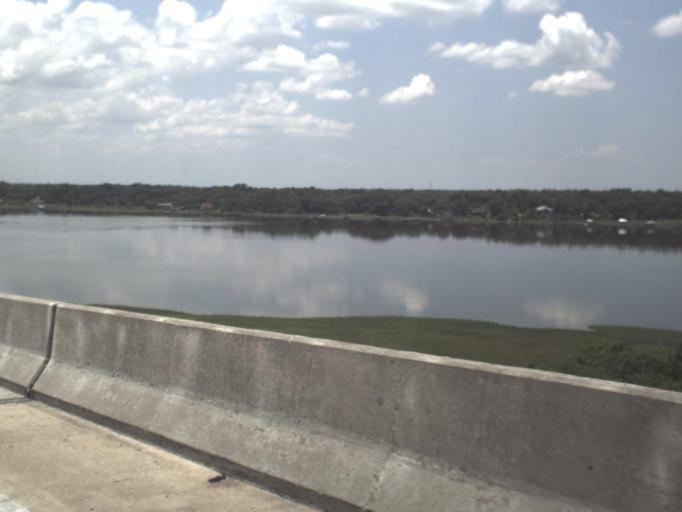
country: US
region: Florida
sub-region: Duval County
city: Jacksonville
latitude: 30.3788
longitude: -81.5546
